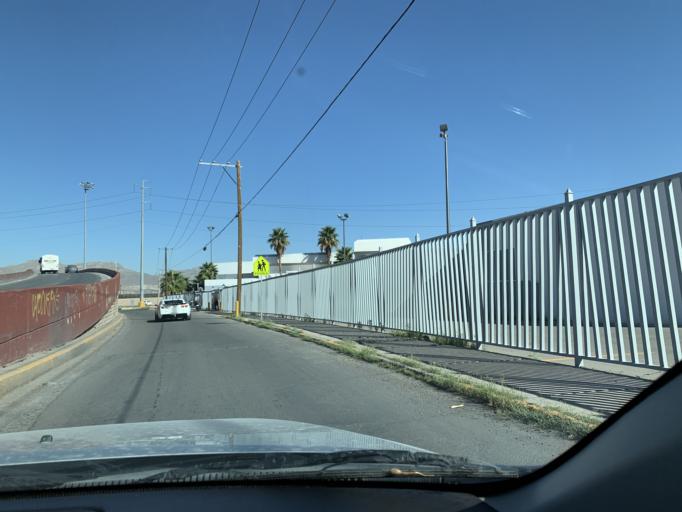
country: MX
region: Chihuahua
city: Ciudad Juarez
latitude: 31.7514
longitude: -106.4267
